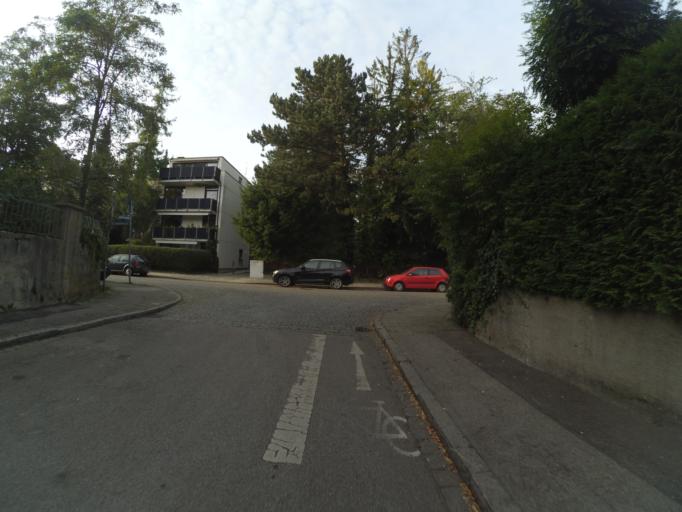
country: DE
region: Bavaria
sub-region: Upper Bavaria
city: Pasing
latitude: 48.1517
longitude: 11.5125
